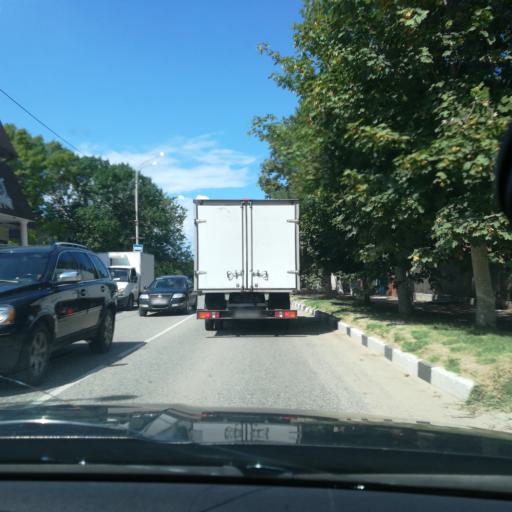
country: RU
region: Krasnodarskiy
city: Taman'
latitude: 45.2174
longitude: 36.7316
